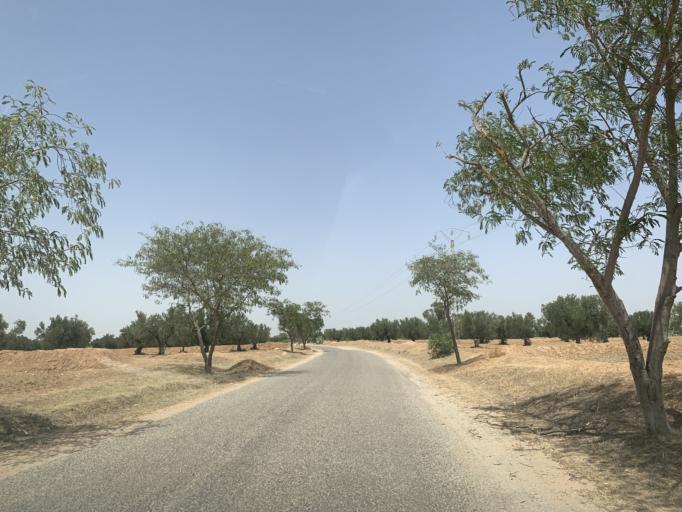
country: TN
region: Al Mahdiyah
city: Shurban
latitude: 35.1847
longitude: 10.2418
